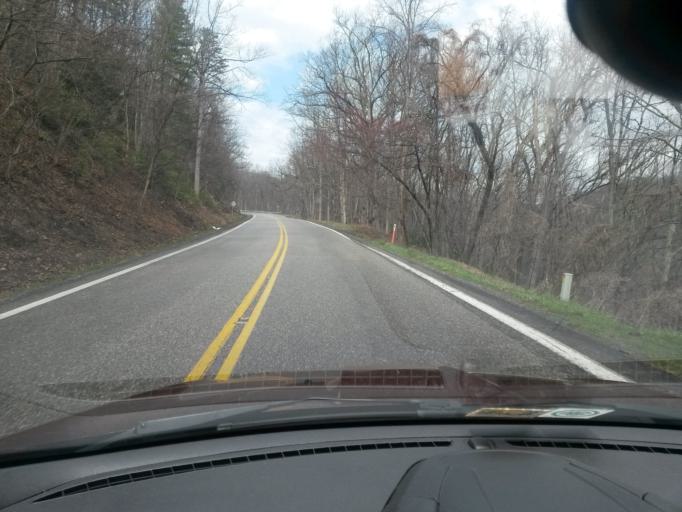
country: US
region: Virginia
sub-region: Bath County
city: Warm Springs
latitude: 38.0470
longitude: -79.7486
